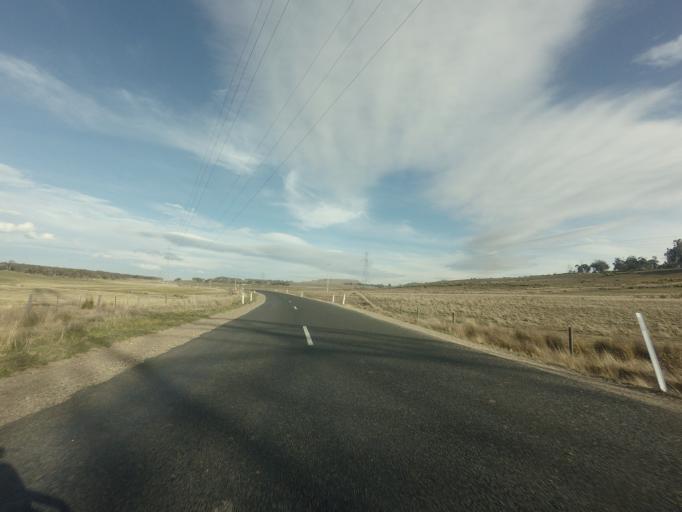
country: AU
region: Tasmania
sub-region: Derwent Valley
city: New Norfolk
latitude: -42.2612
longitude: 146.9376
